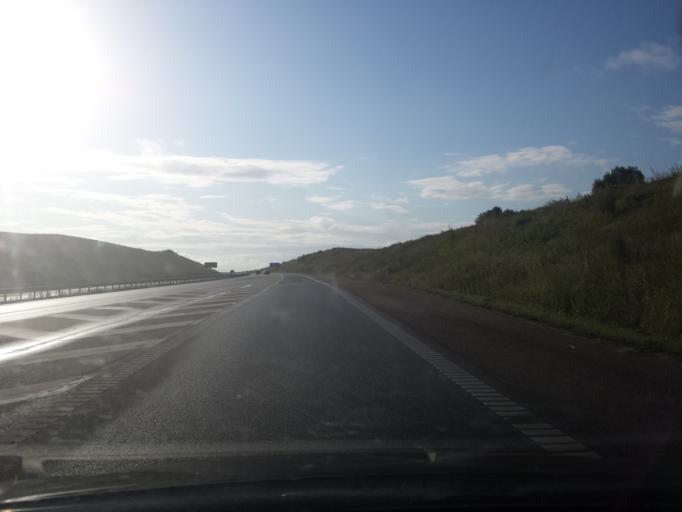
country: DK
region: South Denmark
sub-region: Sonderborg Kommune
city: Dybbol
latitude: 54.9224
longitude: 9.7300
